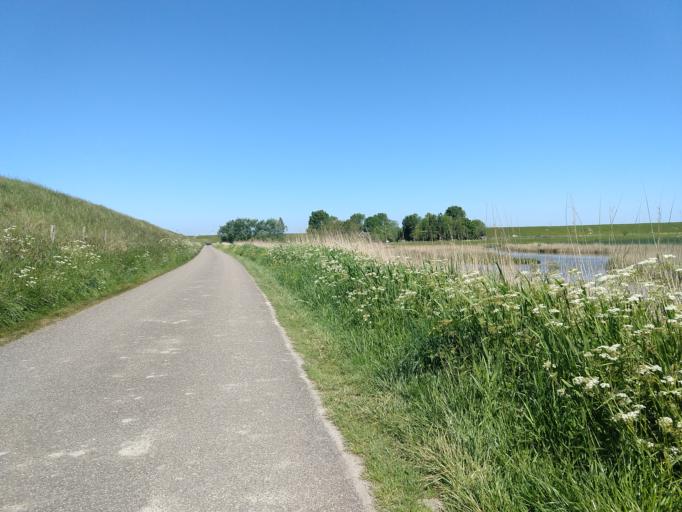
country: NL
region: Zeeland
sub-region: Gemeente Noord-Beveland
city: Kamperland
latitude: 51.5935
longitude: 3.7512
